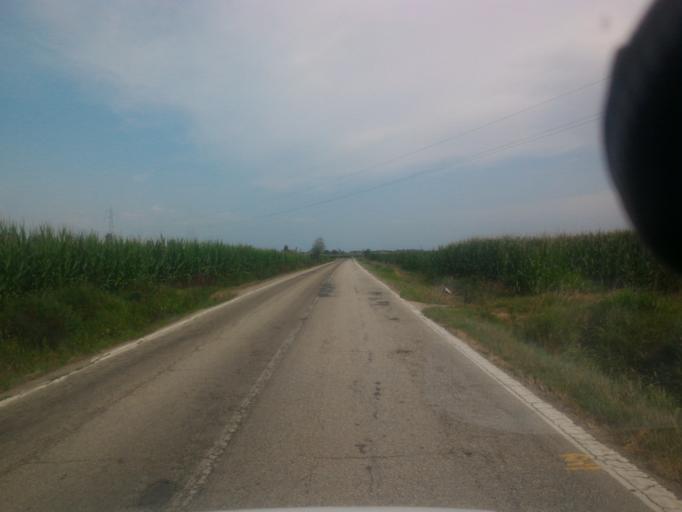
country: IT
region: Piedmont
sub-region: Provincia di Torino
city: Vigone
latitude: 44.8507
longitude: 7.4667
